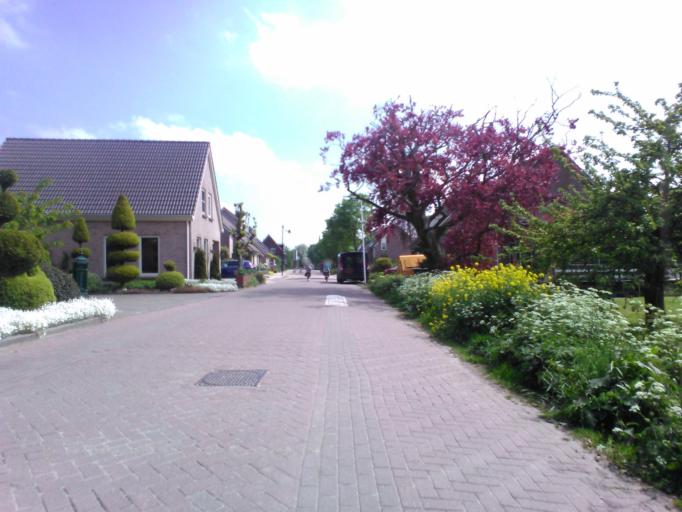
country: NL
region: South Holland
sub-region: Gemeente Rijnwoude
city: Benthuizen
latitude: 52.0969
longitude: 4.5760
